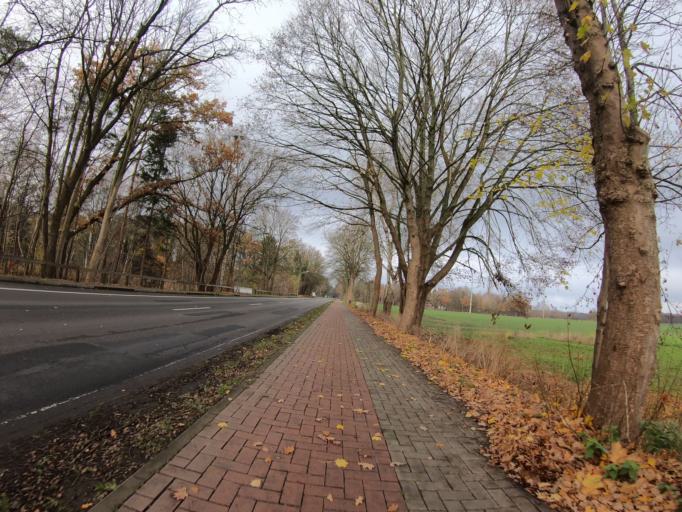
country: DE
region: Lower Saxony
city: Wagenhoff
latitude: 52.5329
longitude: 10.5235
